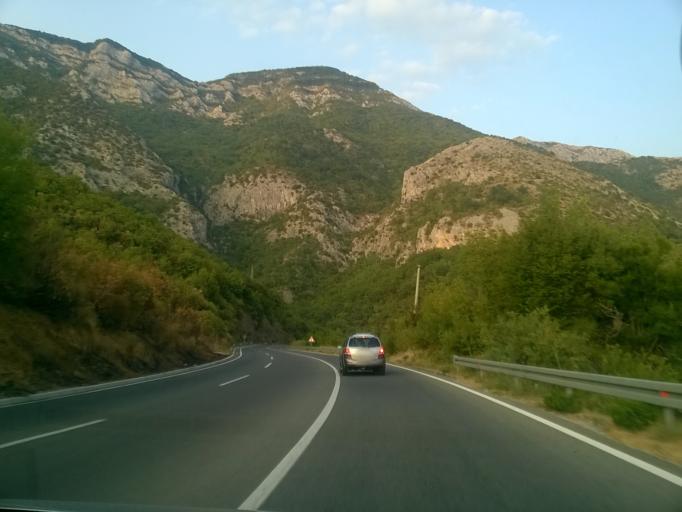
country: ME
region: Bar
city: Sutomore
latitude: 42.1723
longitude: 19.0042
